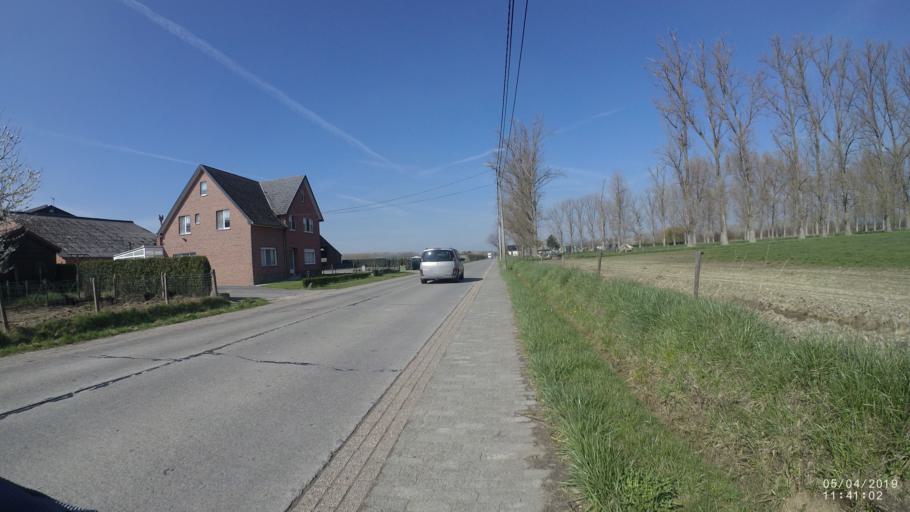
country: BE
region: Flanders
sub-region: Provincie Vlaams-Brabant
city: Geetbets
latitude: 50.8962
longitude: 5.1533
